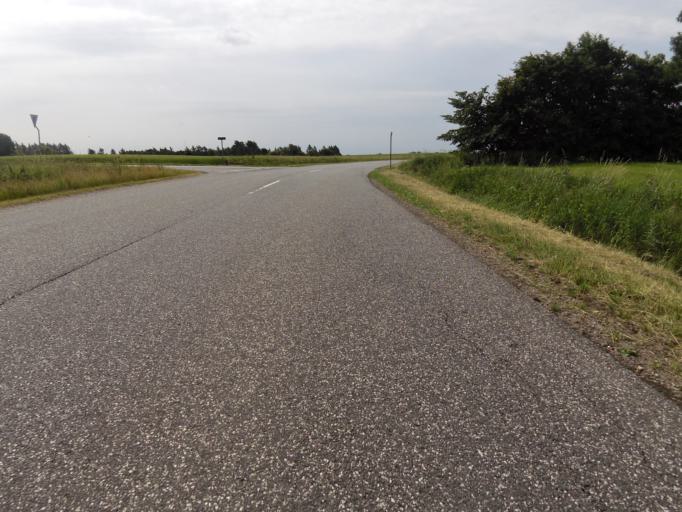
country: DK
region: Central Jutland
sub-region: Holstebro Kommune
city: Holstebro
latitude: 56.4307
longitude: 8.6308
